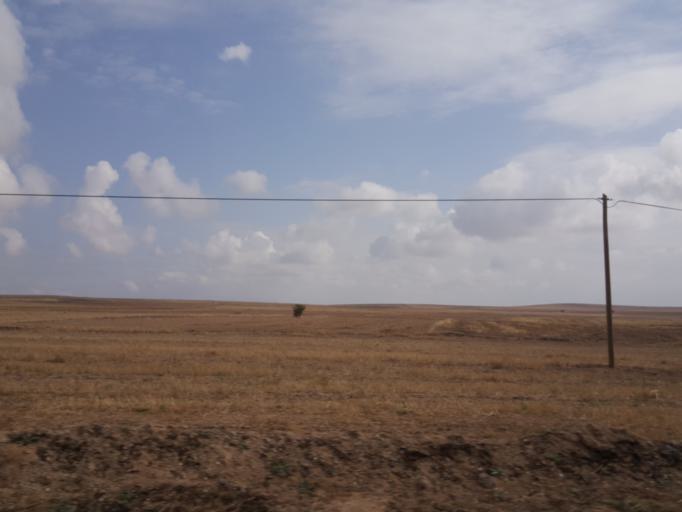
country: TR
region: Kirikkale
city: Keskin
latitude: 39.6174
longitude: 33.6128
